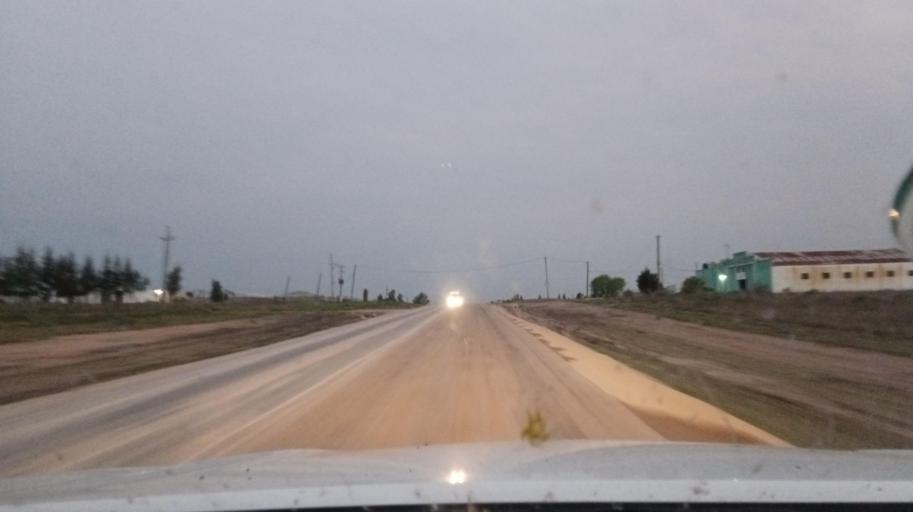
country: UY
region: Canelones
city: Santa Rosa
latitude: -34.5622
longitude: -56.1017
